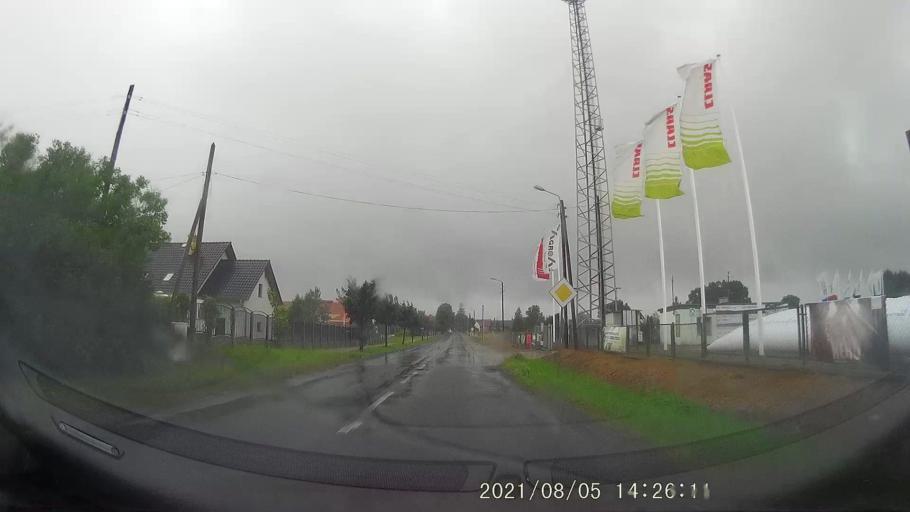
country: PL
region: Opole Voivodeship
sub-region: Powiat nyski
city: Korfantow
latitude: 50.4870
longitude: 17.6053
